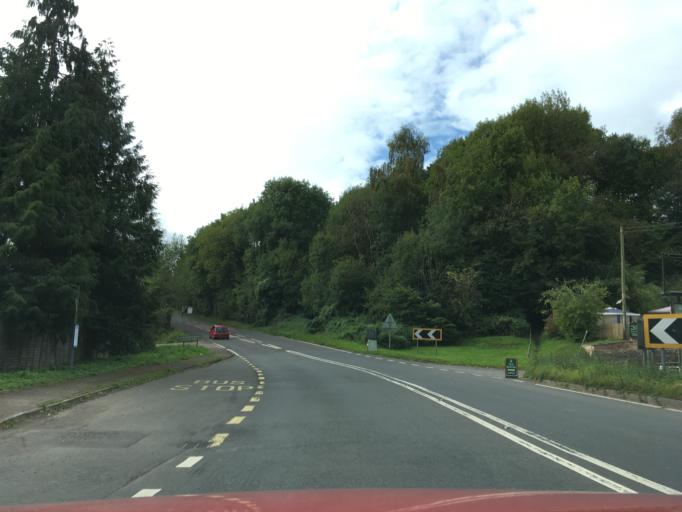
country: GB
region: England
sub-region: Gloucestershire
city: Bream
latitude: 51.7014
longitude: -2.5813
